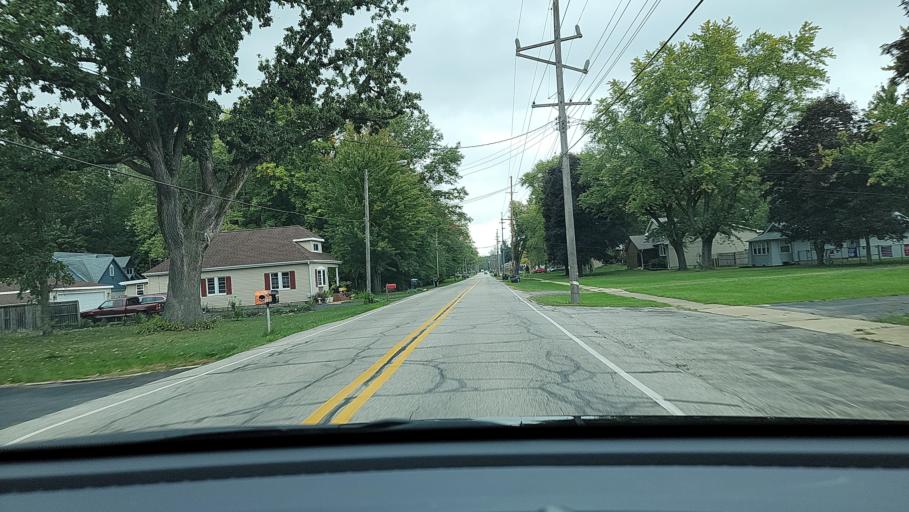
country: US
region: Indiana
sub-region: Porter County
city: Portage
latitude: 41.5669
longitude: -87.2023
